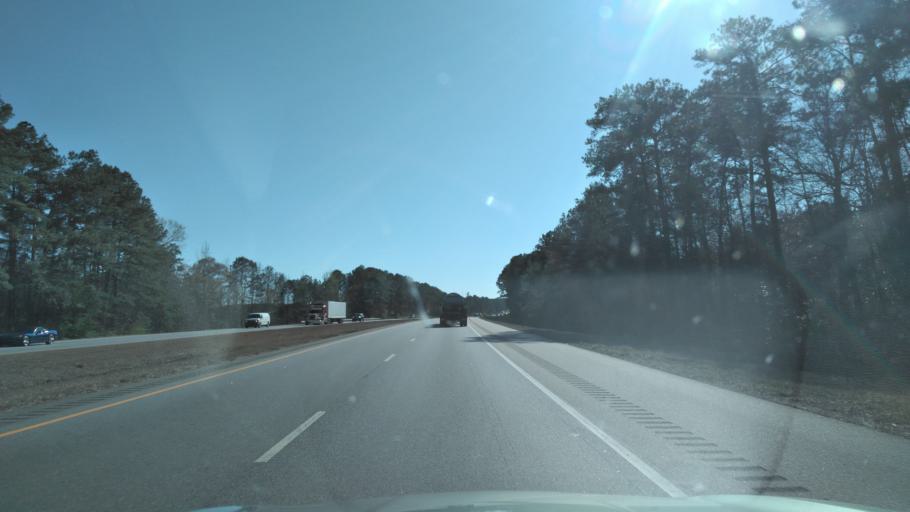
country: US
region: Alabama
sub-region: Butler County
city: Greenville
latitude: 31.7853
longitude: -86.6796
